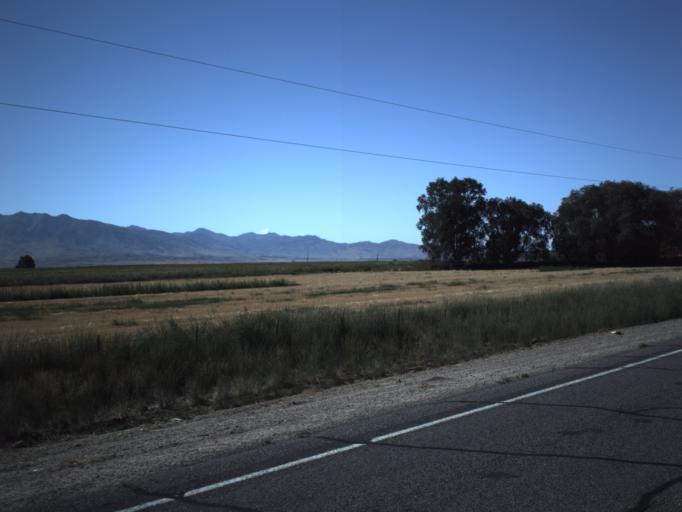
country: US
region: Utah
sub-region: Millard County
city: Delta
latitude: 39.5419
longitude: -112.3622
